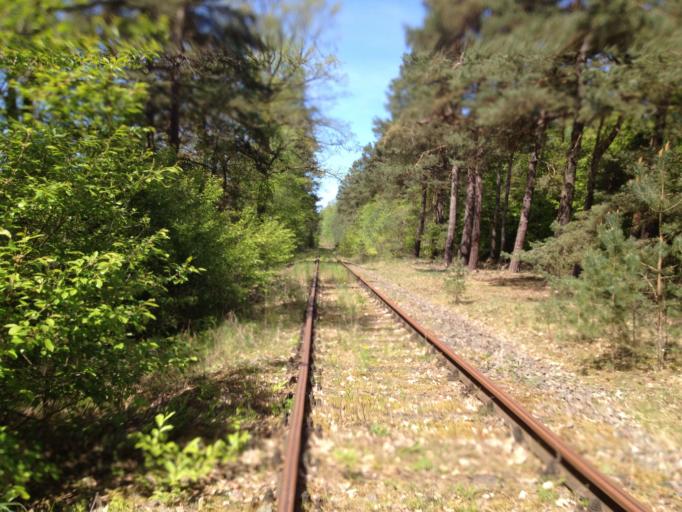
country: DE
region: Brandenburg
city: Lychen
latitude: 53.1556
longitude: 13.3915
